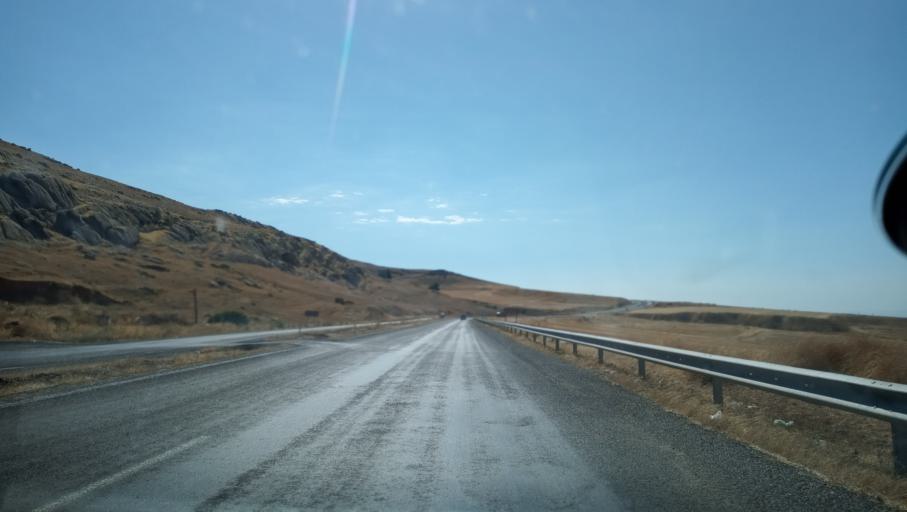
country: TR
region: Diyarbakir
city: Silvan
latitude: 38.1329
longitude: 41.0445
